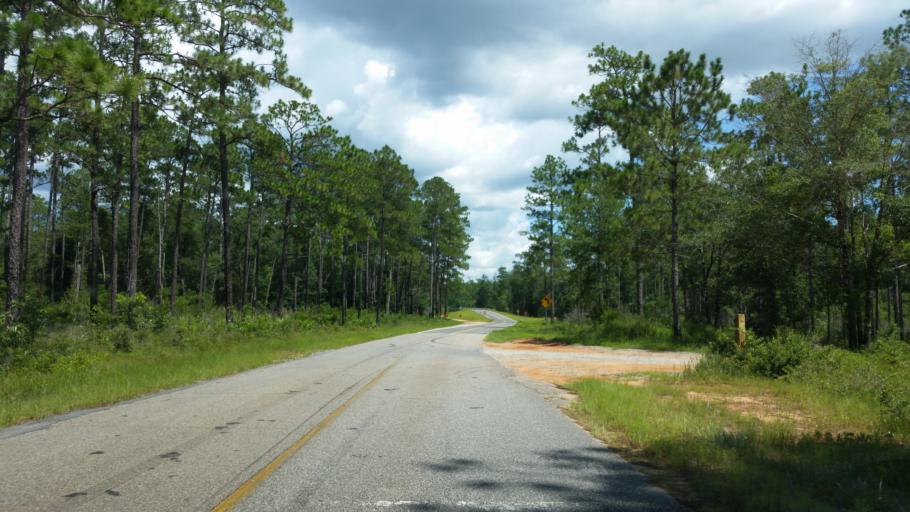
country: US
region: Florida
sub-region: Okaloosa County
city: Crestview
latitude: 30.7260
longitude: -86.7965
